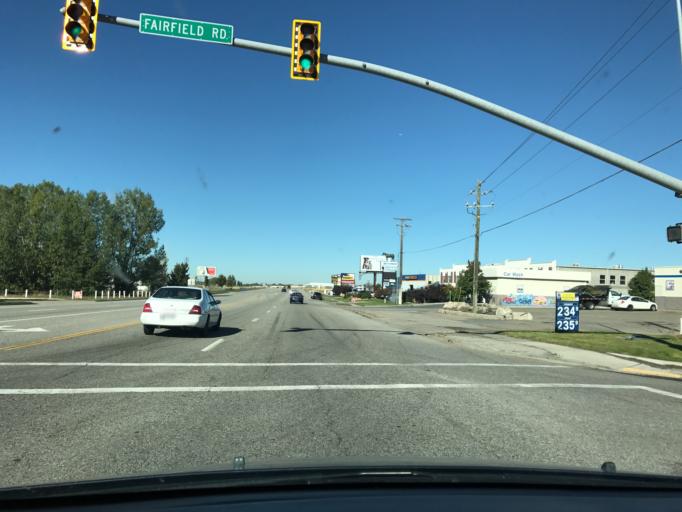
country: US
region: Utah
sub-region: Davis County
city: Hill Air Force Bace
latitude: 41.1026
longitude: -111.9501
